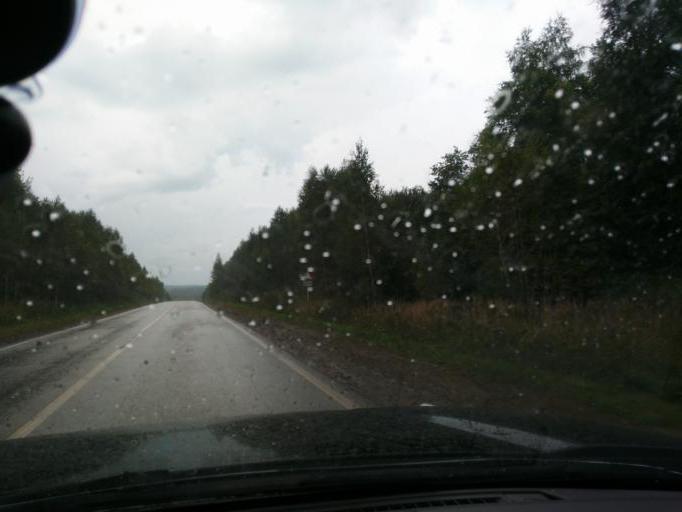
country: RU
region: Perm
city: Barda
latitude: 56.8687
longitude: 55.8915
